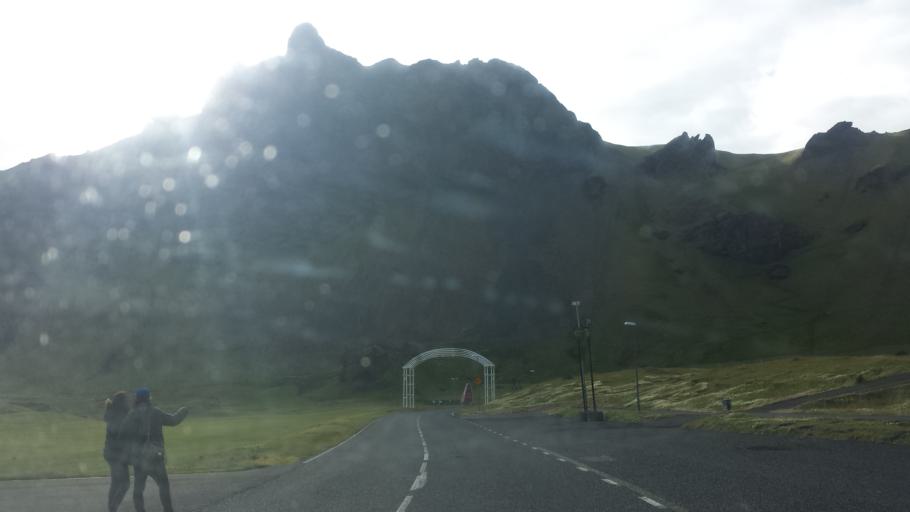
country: IS
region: South
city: Vestmannaeyjar
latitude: 63.4410
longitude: -20.2950
